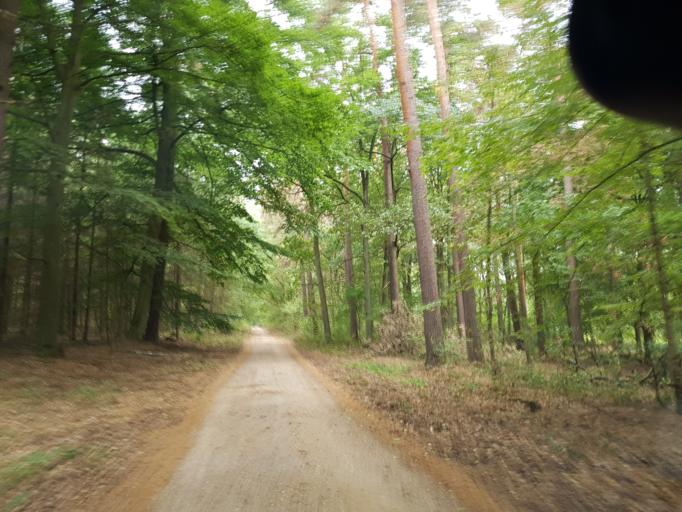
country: DE
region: Saxony-Anhalt
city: Rosslau
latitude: 52.0171
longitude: 12.2932
